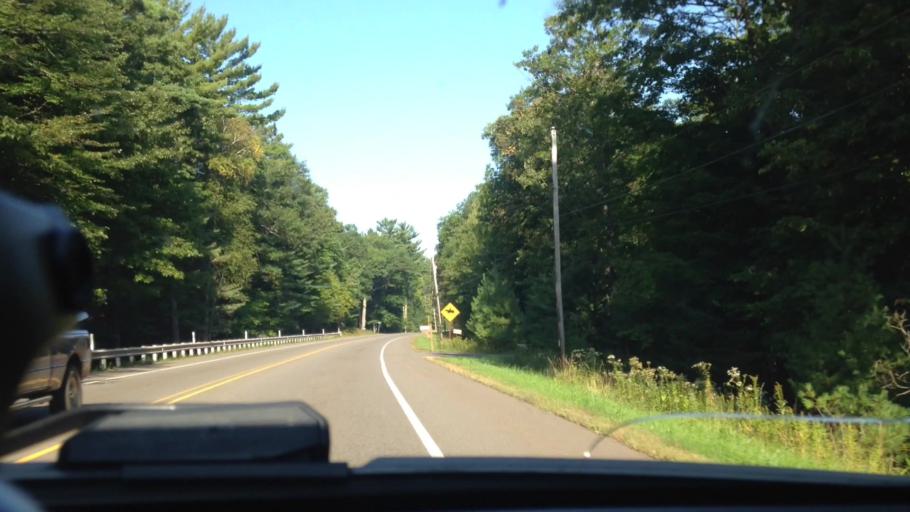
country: US
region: Michigan
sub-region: Dickinson County
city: Quinnesec
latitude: 45.8321
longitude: -88.0038
